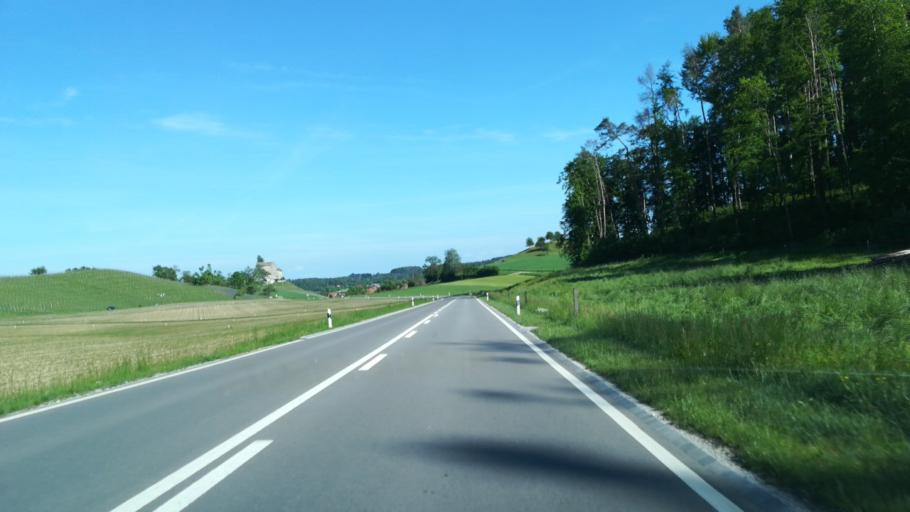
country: CH
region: Thurgau
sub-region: Frauenfeld District
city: Diessenhofen
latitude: 47.6260
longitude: 8.7684
